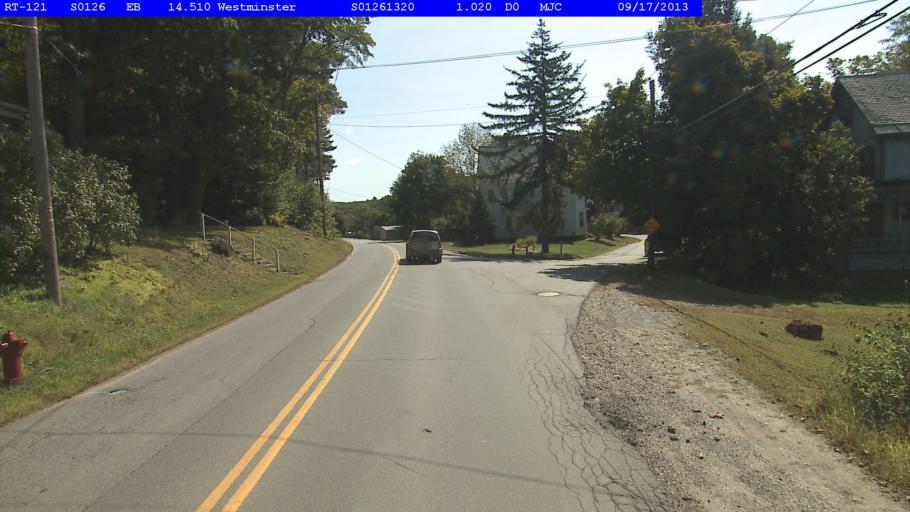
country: US
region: Vermont
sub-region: Windham County
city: Bellows Falls
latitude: 43.1202
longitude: -72.4593
